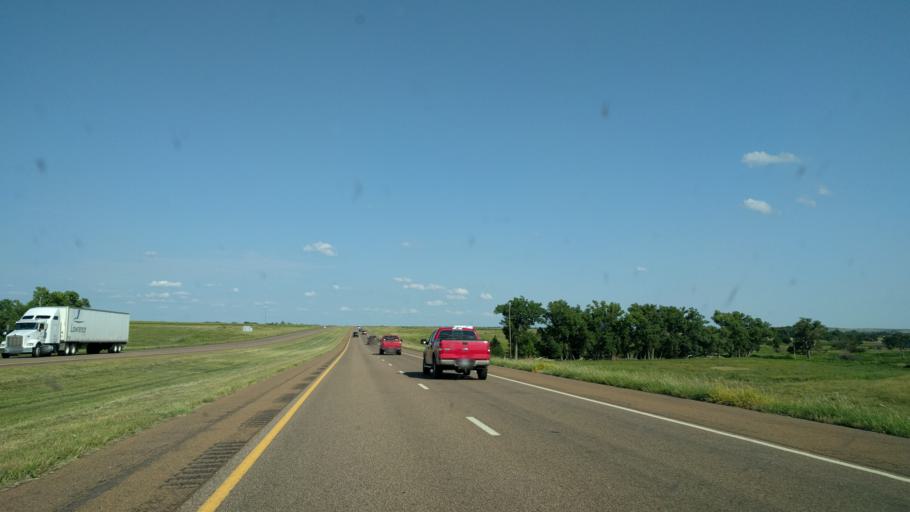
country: US
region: Kansas
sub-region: Ellis County
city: Ellis
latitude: 38.9624
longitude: -99.6342
